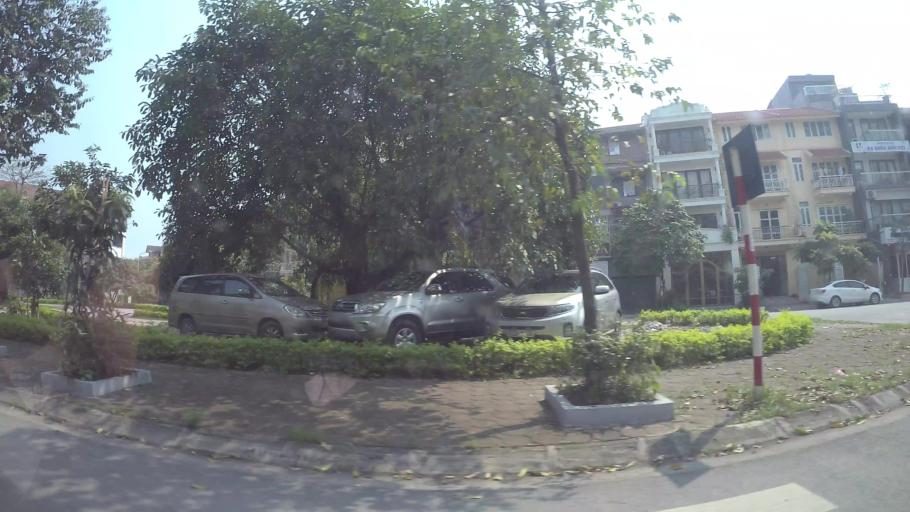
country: VN
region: Ha Noi
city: Ha Dong
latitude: 20.9730
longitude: 105.7971
